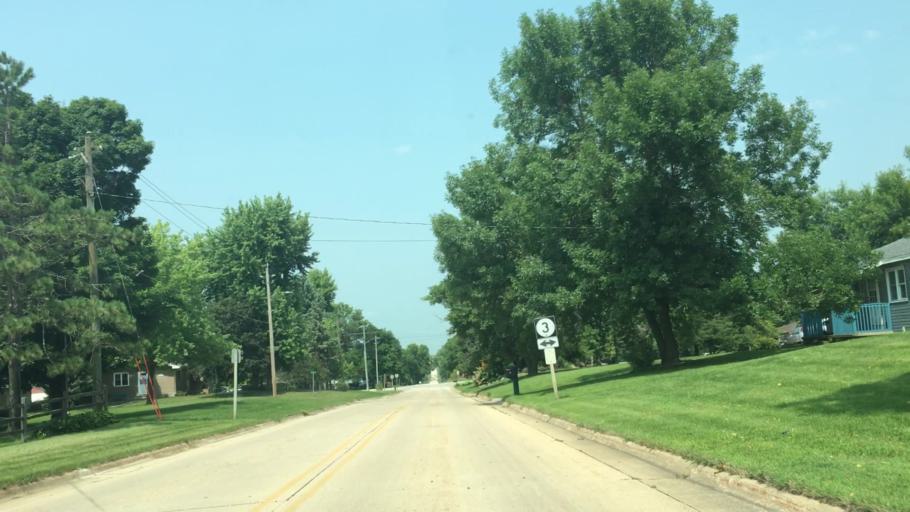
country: US
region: Iowa
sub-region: Fayette County
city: Oelwein
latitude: 42.6775
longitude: -91.8936
